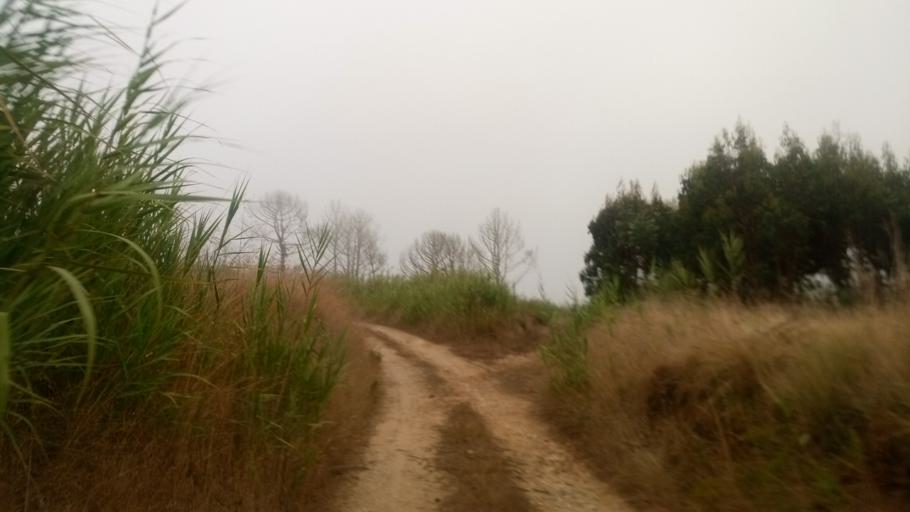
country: PT
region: Leiria
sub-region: Caldas da Rainha
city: Caldas da Rainha
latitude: 39.4671
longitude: -9.1970
